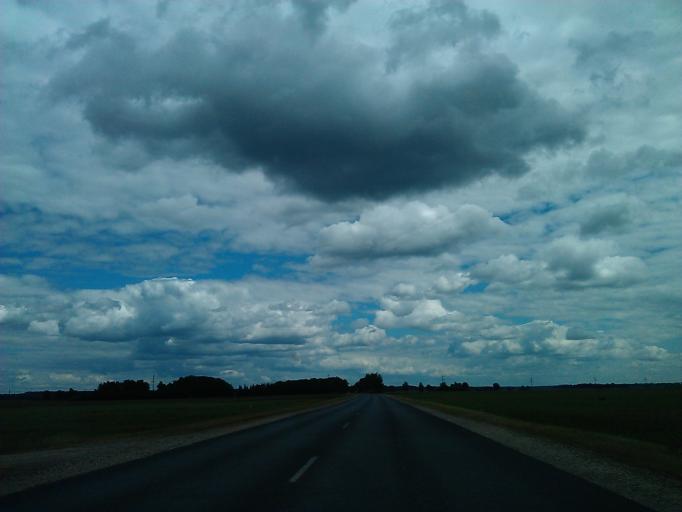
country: LV
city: Tervete
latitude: 56.6219
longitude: 23.4814
